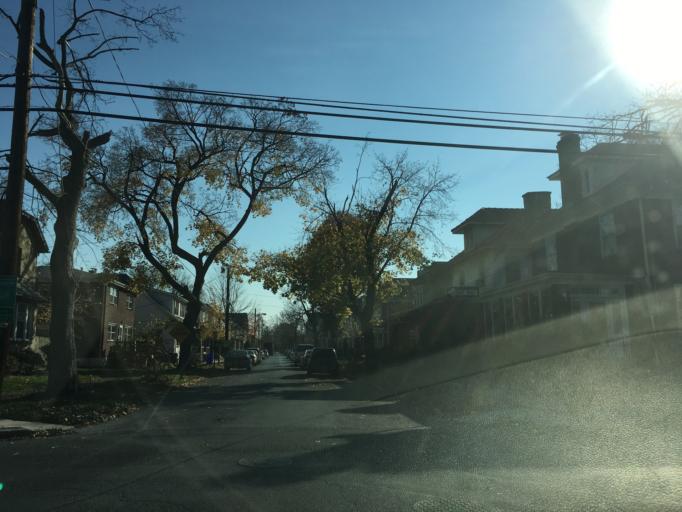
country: US
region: Pennsylvania
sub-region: Dauphin County
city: Harrisburg
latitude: 40.2836
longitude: -76.8994
